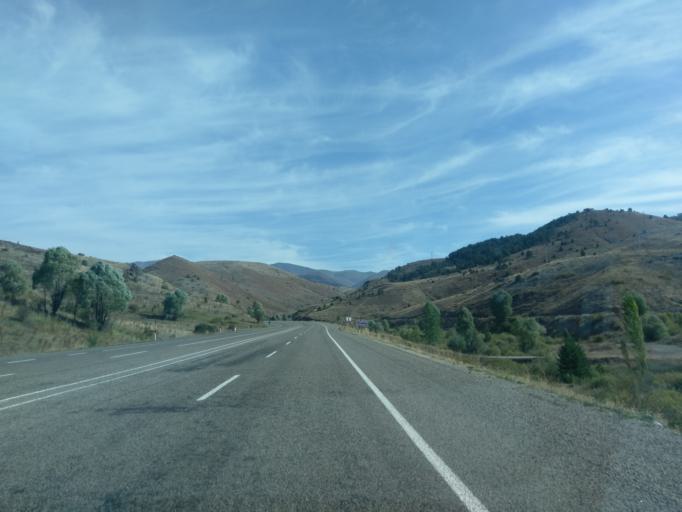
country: TR
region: Sivas
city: Imranli
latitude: 39.8471
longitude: 38.2919
